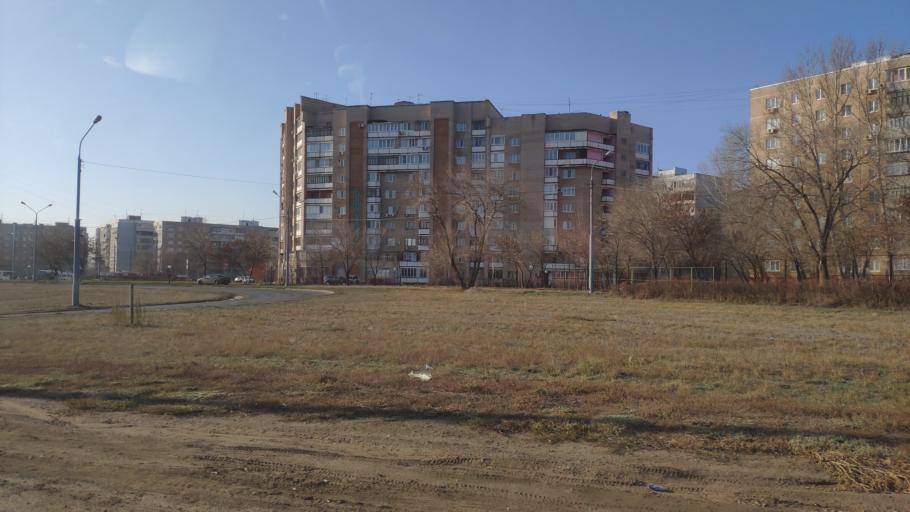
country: RU
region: Orenburg
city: Prigorodnyy
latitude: 51.7759
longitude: 55.1927
